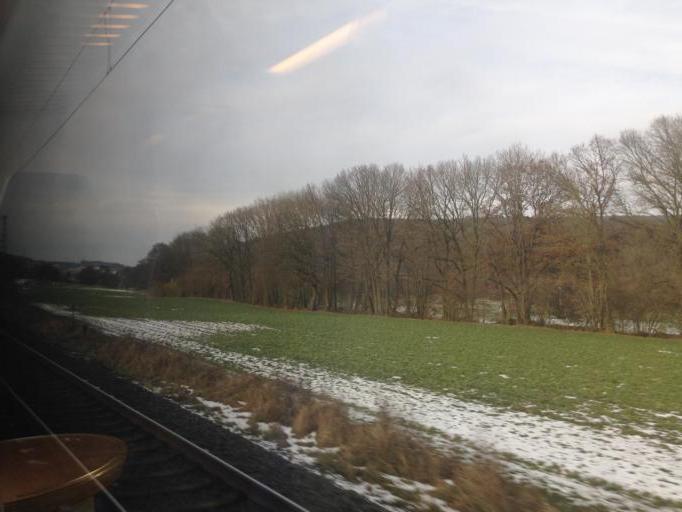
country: DE
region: Hesse
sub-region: Regierungsbezirk Giessen
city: Sinn
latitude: 50.6240
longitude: 8.3310
